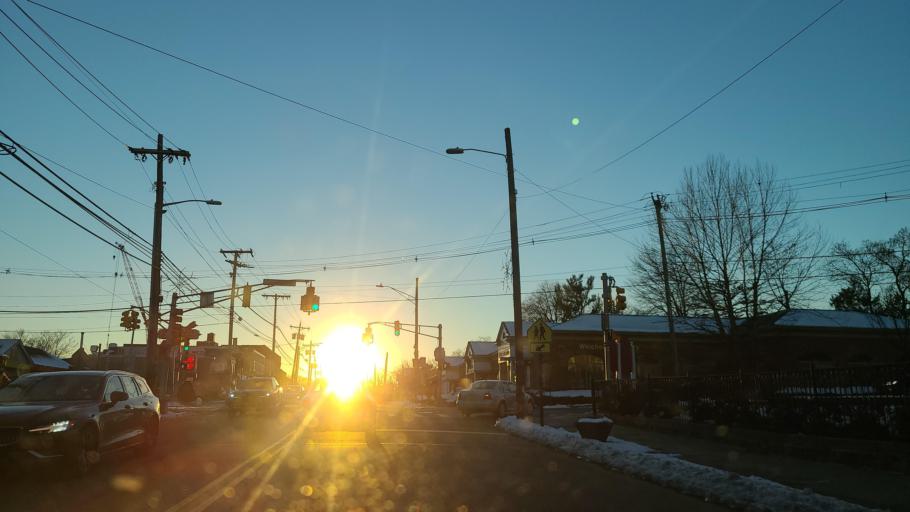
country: US
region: New Jersey
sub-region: Union County
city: Springfield
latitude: 40.7206
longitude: -74.3184
